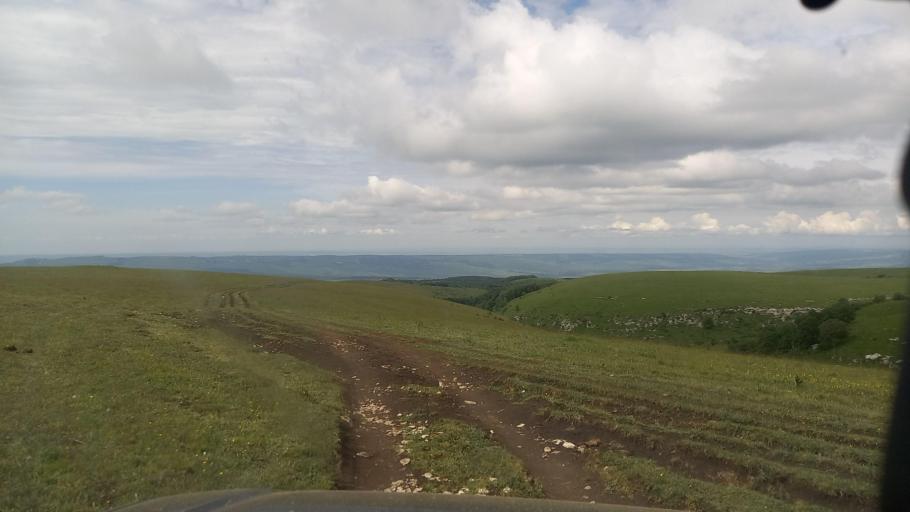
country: RU
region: Karachayevo-Cherkesiya
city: Pregradnaya
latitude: 43.9925
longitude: 41.2708
